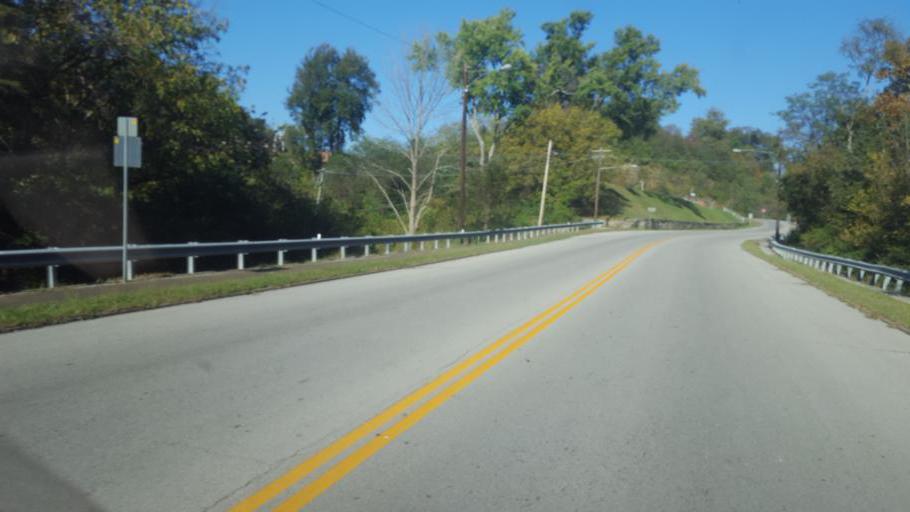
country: US
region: Kentucky
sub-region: Mason County
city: Maysville
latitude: 38.6383
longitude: -83.7549
